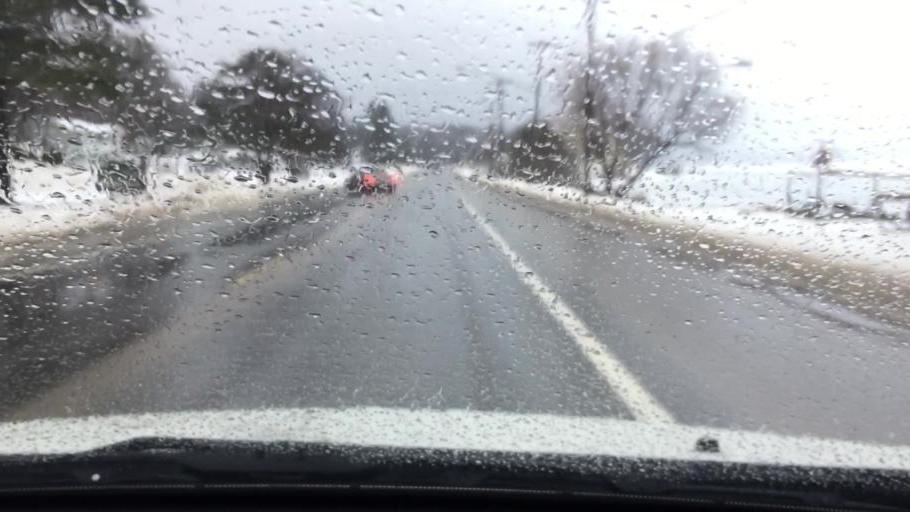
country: US
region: Michigan
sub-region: Charlevoix County
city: East Jordan
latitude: 45.1574
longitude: -85.1444
